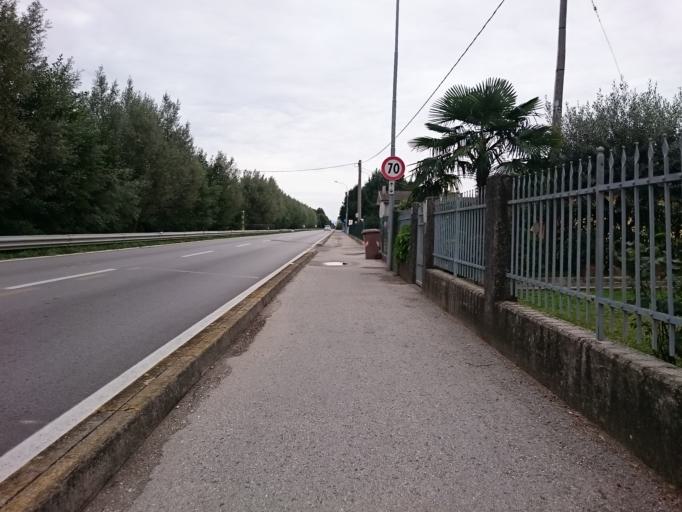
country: IT
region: Veneto
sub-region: Provincia di Vicenza
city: Quinto Vicentino
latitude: 45.5675
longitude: 11.6463
